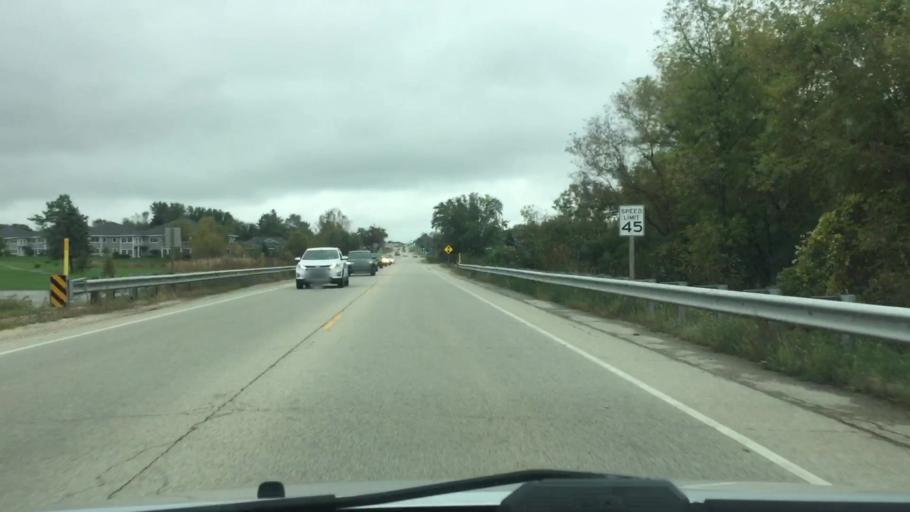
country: US
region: Wisconsin
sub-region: Walworth County
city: Elkhorn
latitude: 42.7100
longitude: -88.5422
